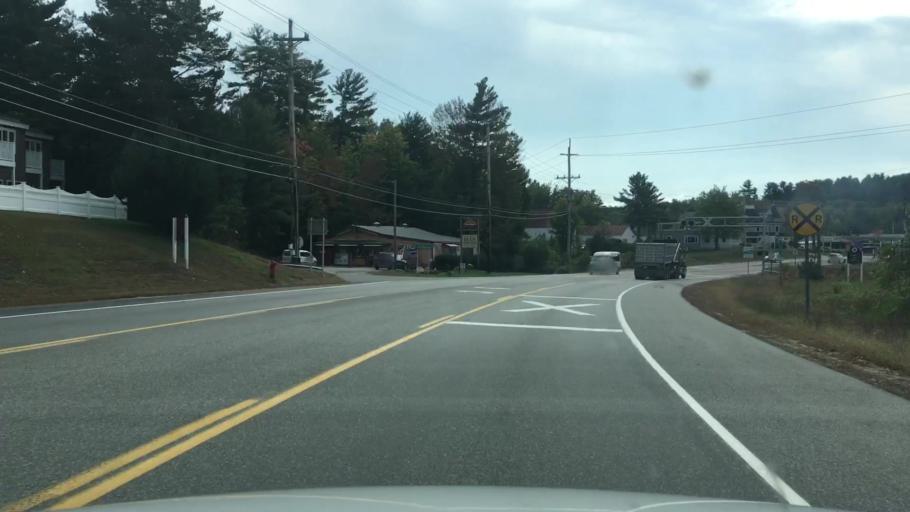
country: US
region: New Hampshire
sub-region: Carroll County
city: North Conway
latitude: 44.0773
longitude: -71.1389
